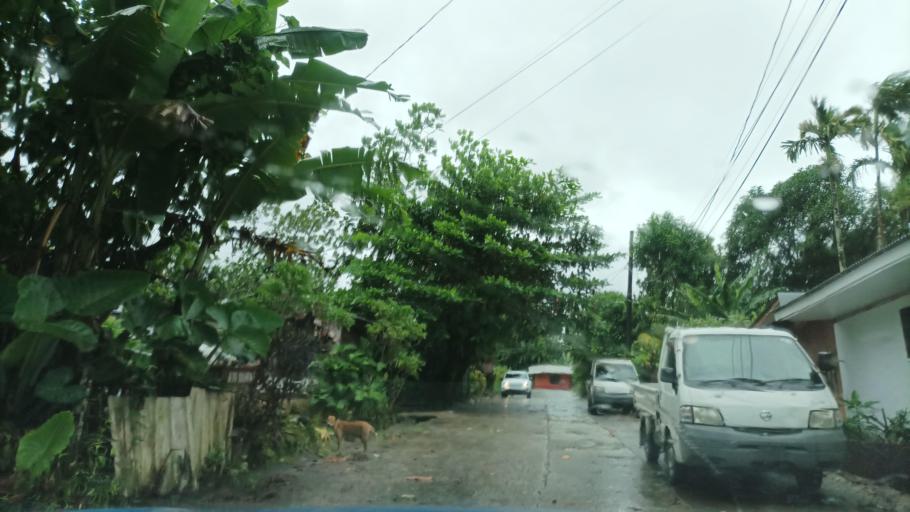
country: FM
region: Pohnpei
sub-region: Kolonia Municipality
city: Kolonia
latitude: 6.9628
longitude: 158.2102
